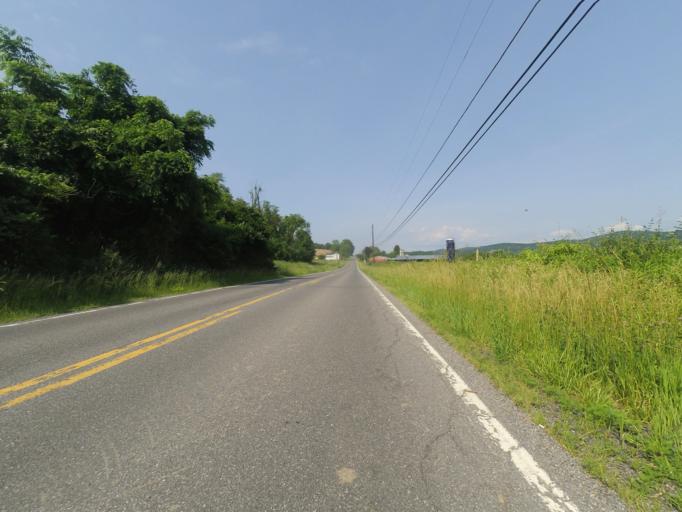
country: US
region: Pennsylvania
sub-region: Centre County
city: Milesburg
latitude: 40.9706
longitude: -77.7302
